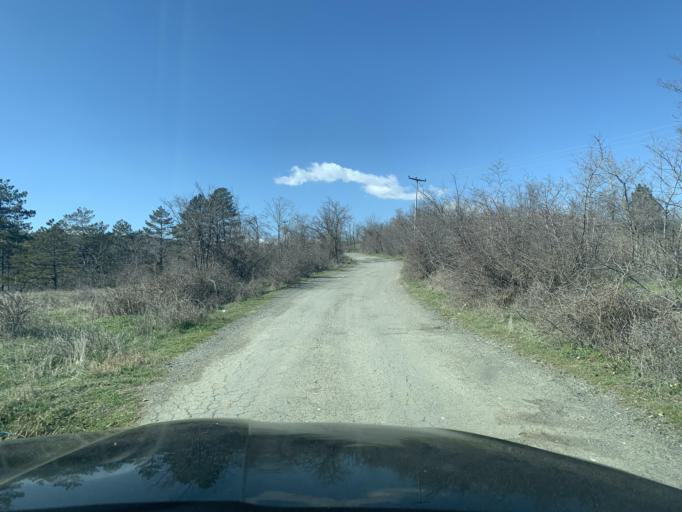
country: MK
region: Demir Kapija
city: Demir Kapija
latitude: 41.4092
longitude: 22.2314
